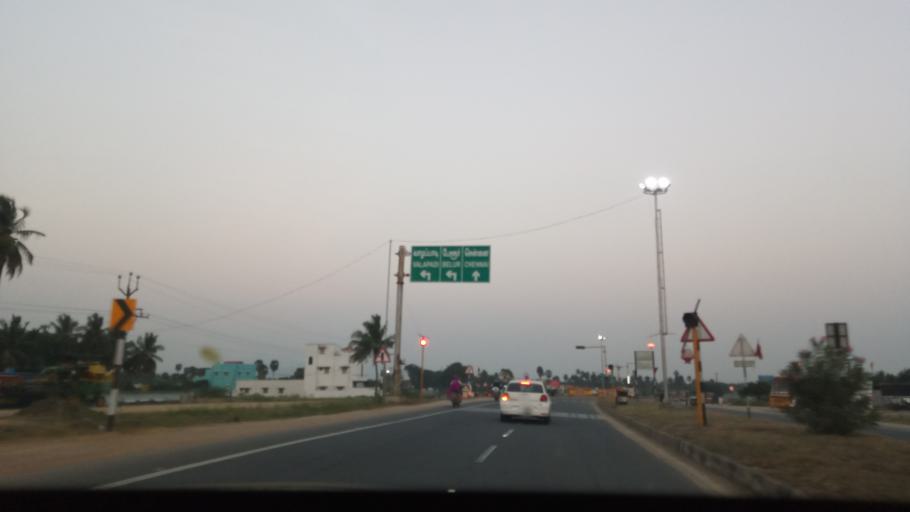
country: IN
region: Tamil Nadu
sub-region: Salem
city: Belur
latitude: 11.6545
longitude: 78.3782
